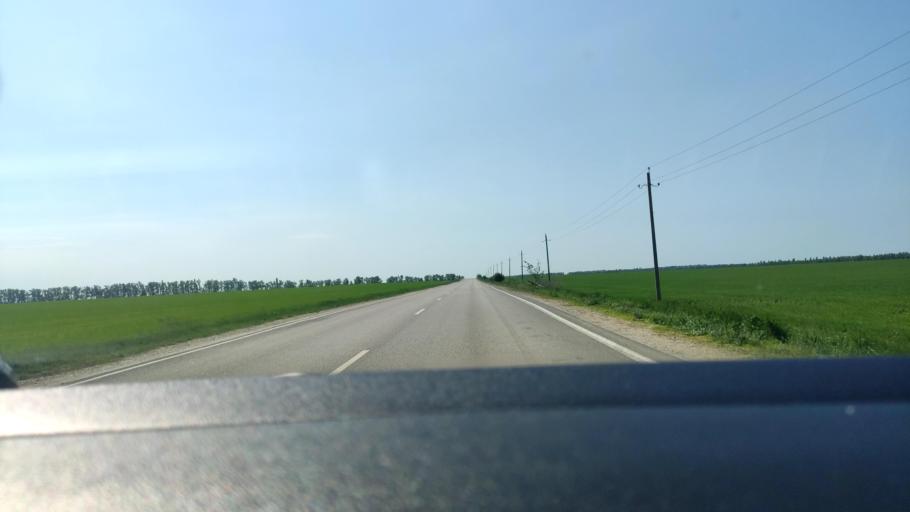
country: RU
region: Voronezj
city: Novaya Usman'
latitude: 51.5644
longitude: 39.3758
